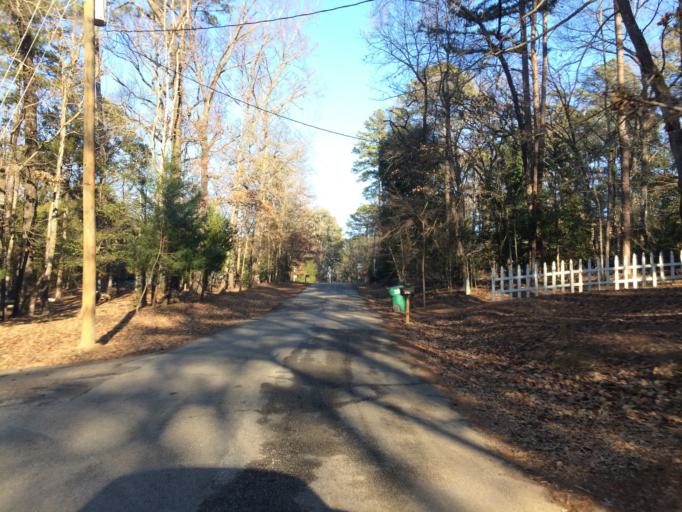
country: US
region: Texas
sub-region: Wood County
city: Hawkins
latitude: 32.7251
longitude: -95.1648
